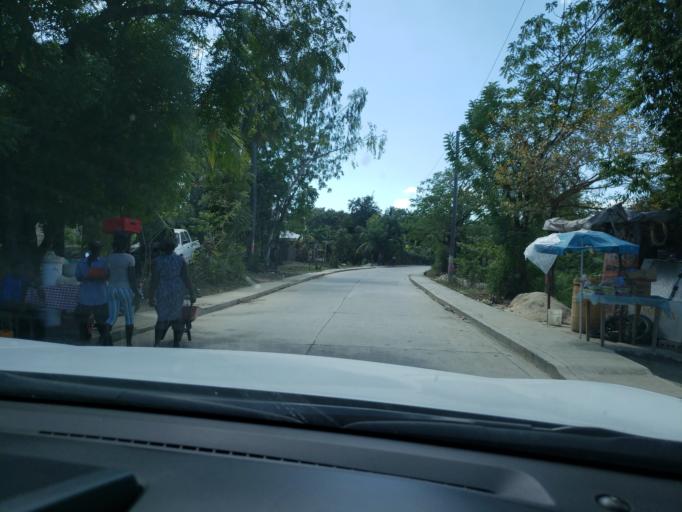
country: HT
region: Grandans
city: Anse-a-Veau
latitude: 18.4514
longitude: -73.3805
